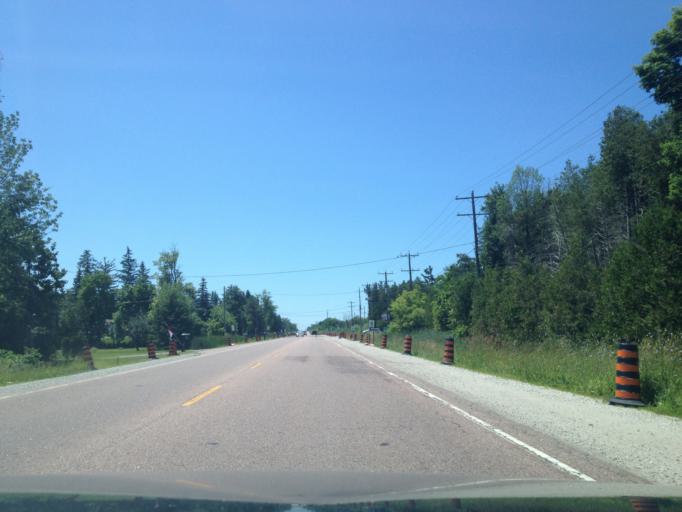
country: CA
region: Ontario
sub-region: Halton
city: Milton
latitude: 43.6709
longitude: -79.9914
